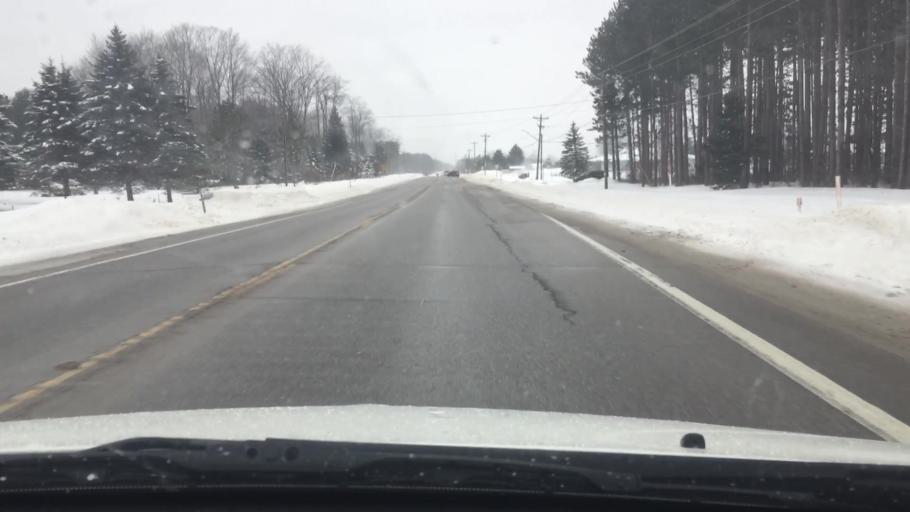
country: US
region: Michigan
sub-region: Otsego County
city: Gaylord
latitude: 45.0276
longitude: -84.7338
